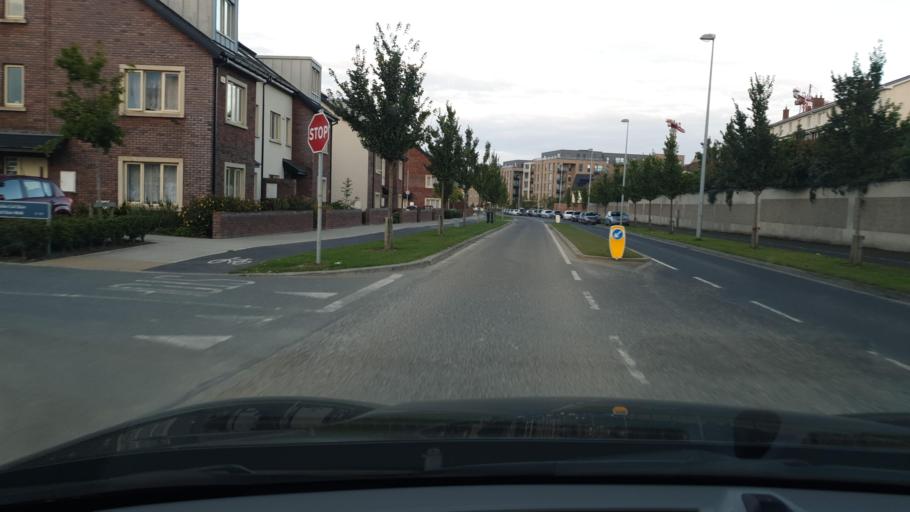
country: IE
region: Leinster
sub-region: South Dublin
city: Saggart
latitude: 53.2849
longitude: -6.4309
